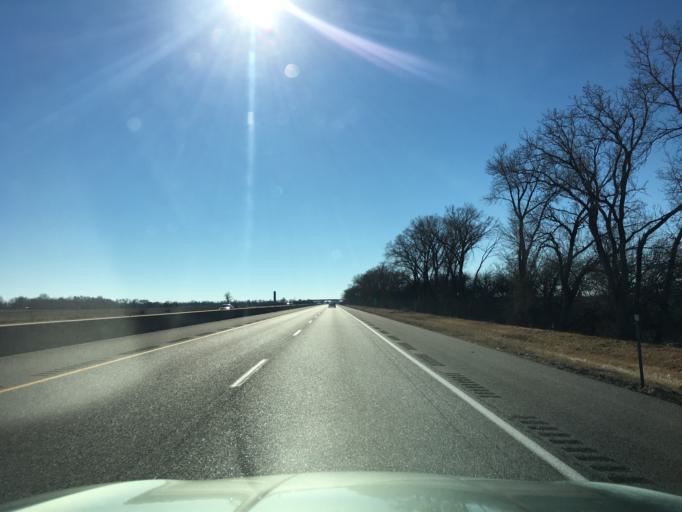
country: US
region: Kansas
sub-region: Sumner County
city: Belle Plaine
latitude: 37.4436
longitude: -97.3219
